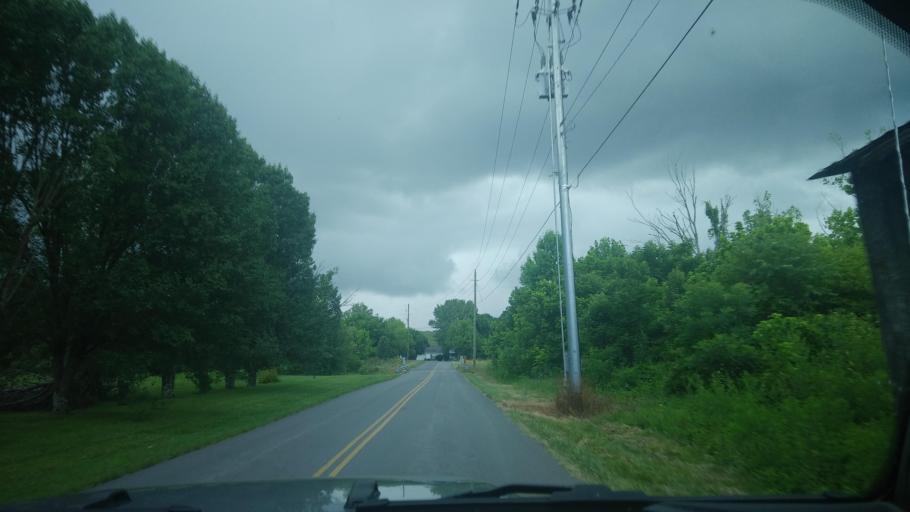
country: US
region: Tennessee
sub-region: Sevier County
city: Pigeon Forge
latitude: 35.7378
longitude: -83.6194
